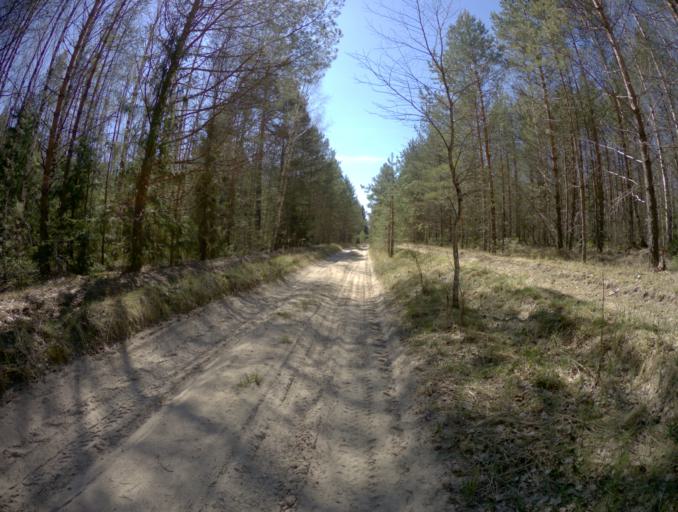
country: RU
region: Vladimir
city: Golovino
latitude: 55.8872
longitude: 40.4078
